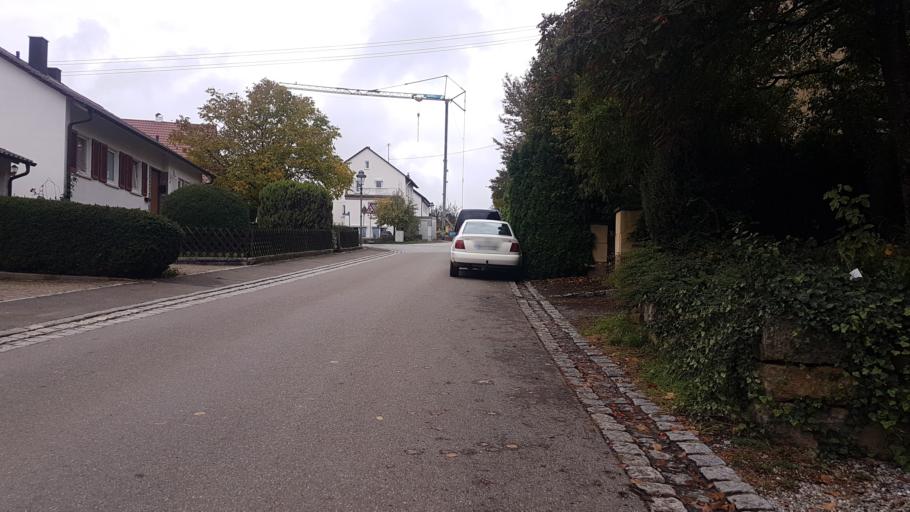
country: DE
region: Baden-Wuerttemberg
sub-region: Tuebingen Region
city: Dusslingen
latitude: 48.4477
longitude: 9.0516
